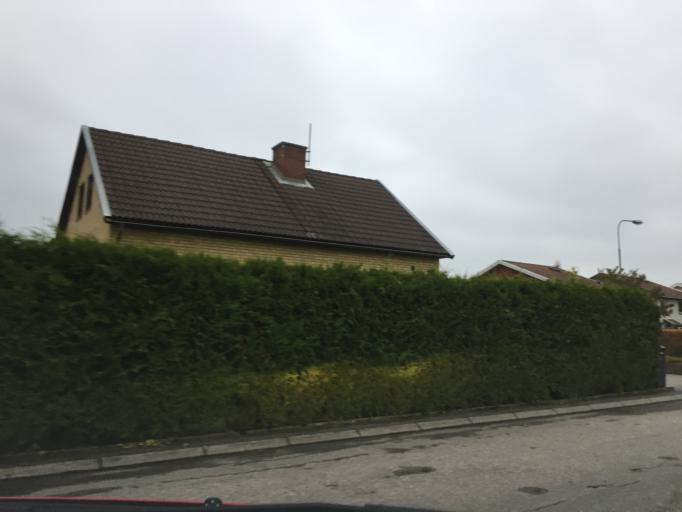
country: SE
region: Vaestra Goetaland
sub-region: Trollhattan
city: Trollhattan
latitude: 58.2571
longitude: 12.2862
